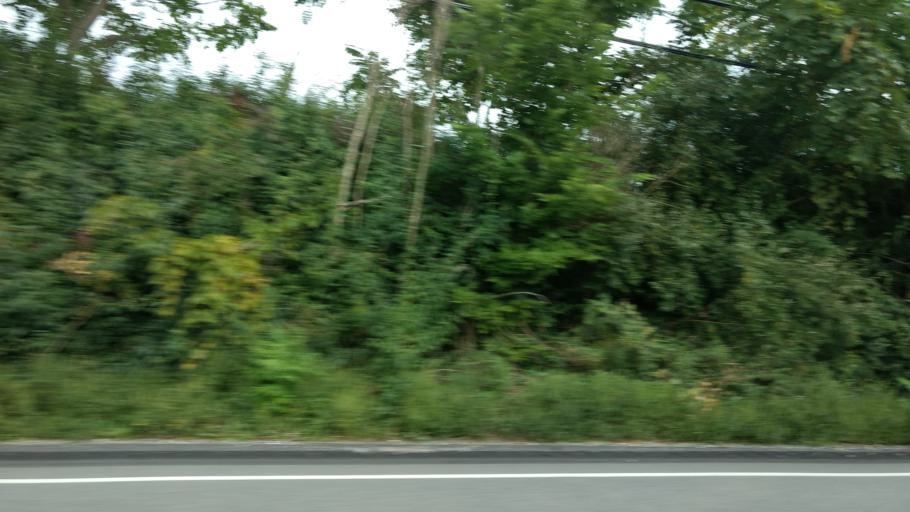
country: US
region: Pennsylvania
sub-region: Westmoreland County
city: Fellsburg
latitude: 40.1653
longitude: -79.8185
